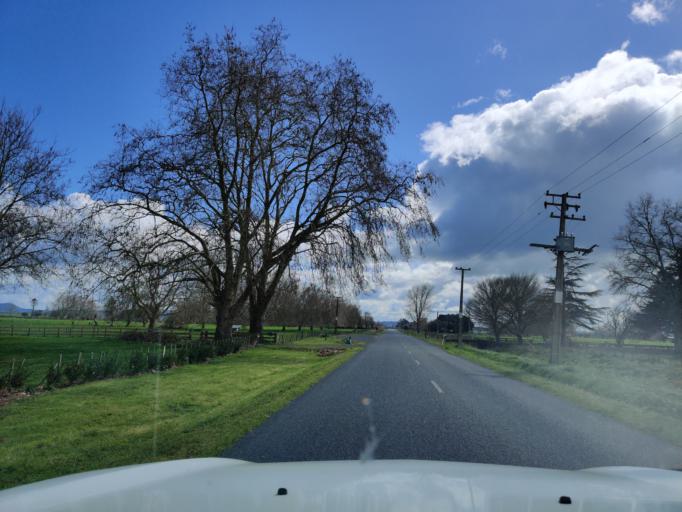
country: NZ
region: Waikato
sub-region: Waikato District
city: Ngaruawahia
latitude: -37.6134
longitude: 175.3124
